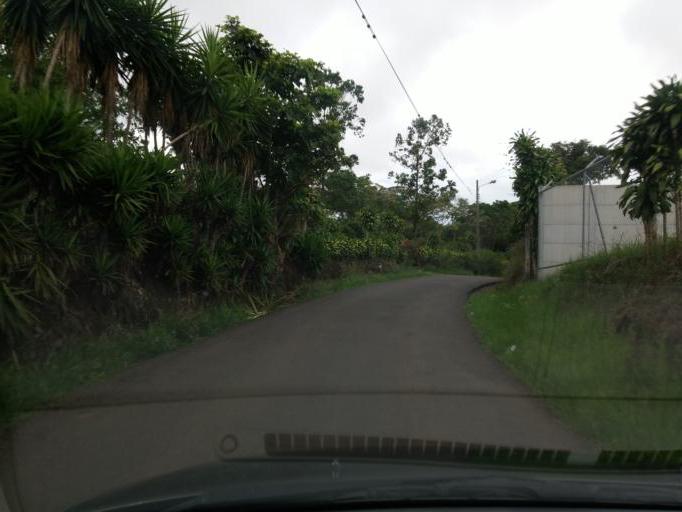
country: CR
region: Heredia
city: Mercedes
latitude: 10.0283
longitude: -84.1318
